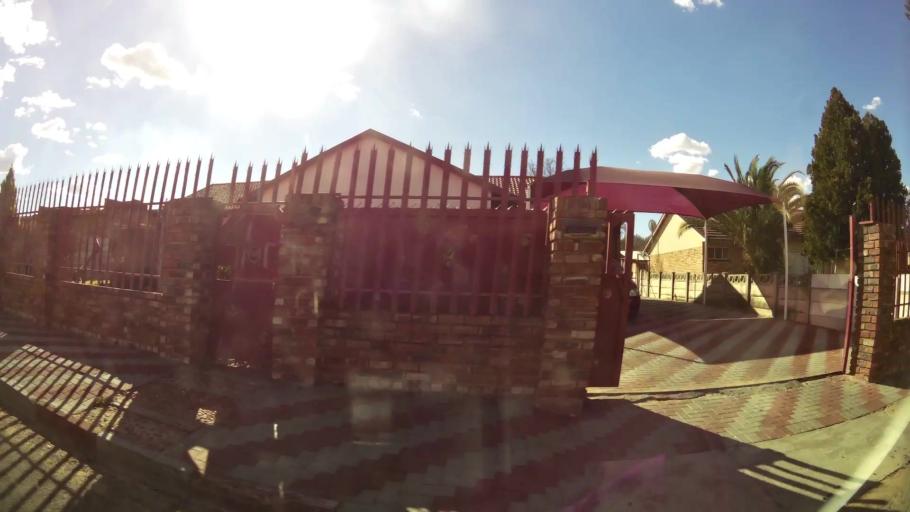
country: ZA
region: North-West
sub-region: Dr Kenneth Kaunda District Municipality
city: Klerksdorp
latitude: -26.8634
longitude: 26.6481
